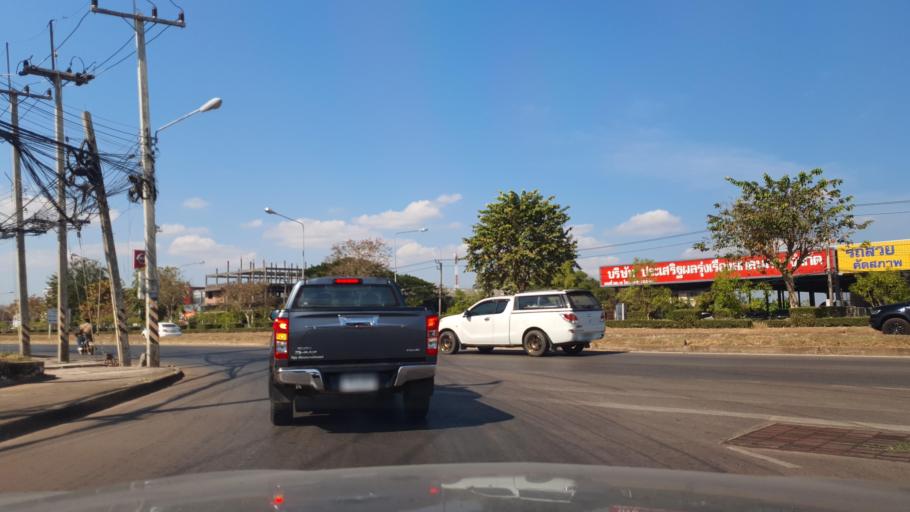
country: TH
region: Sakon Nakhon
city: Sakon Nakhon
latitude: 17.1753
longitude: 104.1281
